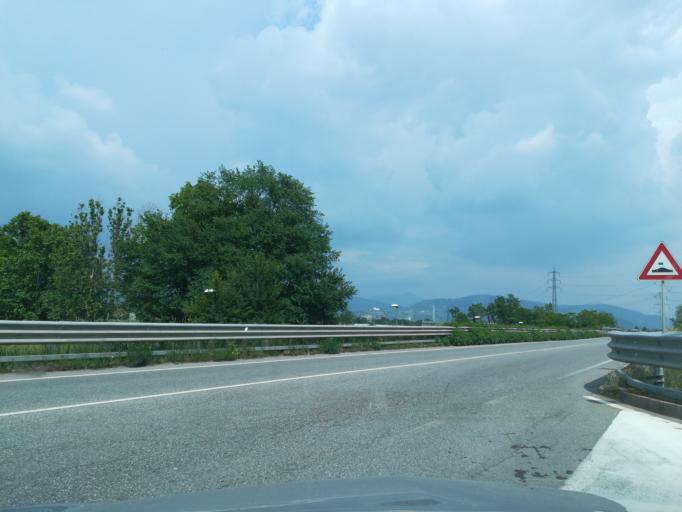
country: IT
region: Lombardy
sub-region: Provincia di Bergamo
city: Bagnatica
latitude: 45.6552
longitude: 9.7863
